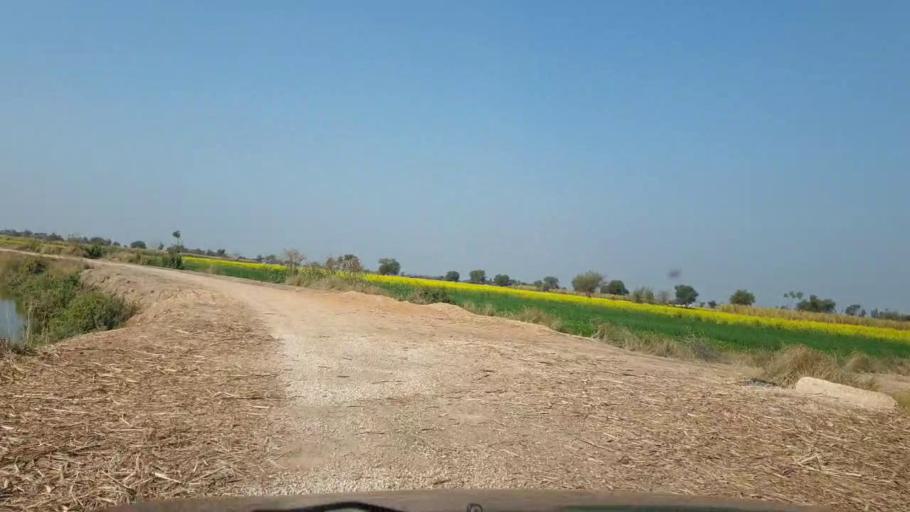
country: PK
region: Sindh
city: Sinjhoro
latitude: 26.0477
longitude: 68.7373
